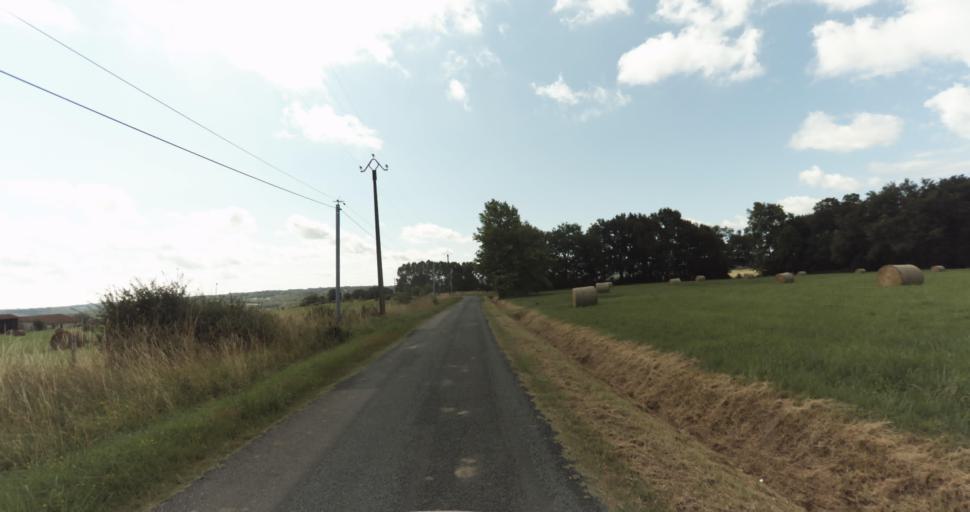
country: FR
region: Aquitaine
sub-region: Departement de la Gironde
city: Bazas
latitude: 44.4521
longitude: -0.1843
